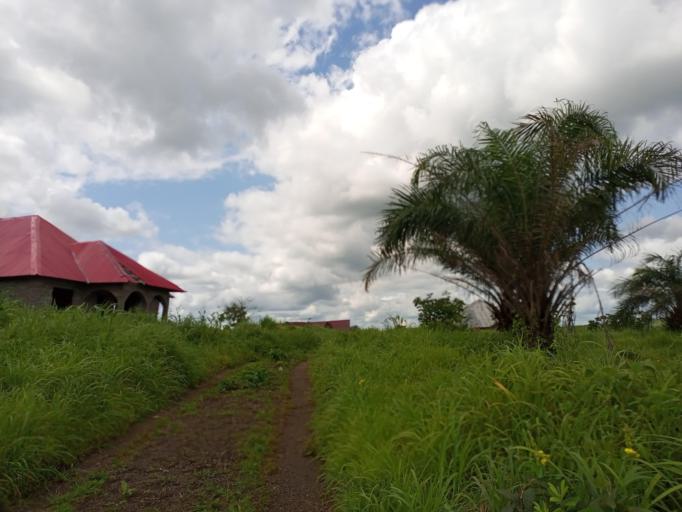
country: SL
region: Northern Province
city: Kamakwie
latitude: 9.5067
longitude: -12.2305
